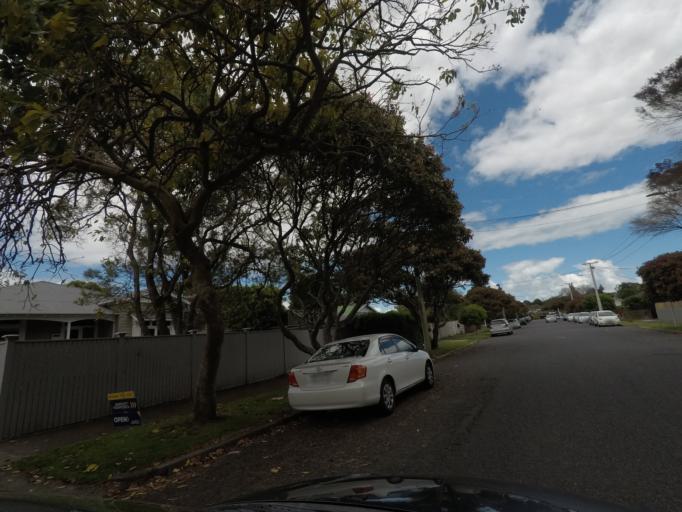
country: NZ
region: Auckland
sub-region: Auckland
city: Auckland
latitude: -36.8883
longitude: 174.7342
